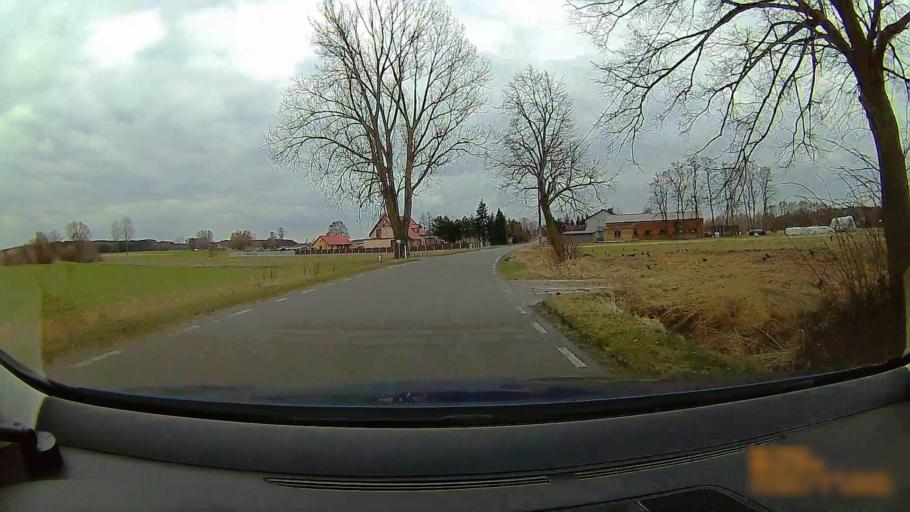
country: PL
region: Greater Poland Voivodeship
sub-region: Powiat koninski
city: Rzgow Pierwszy
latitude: 52.1471
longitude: 18.0552
